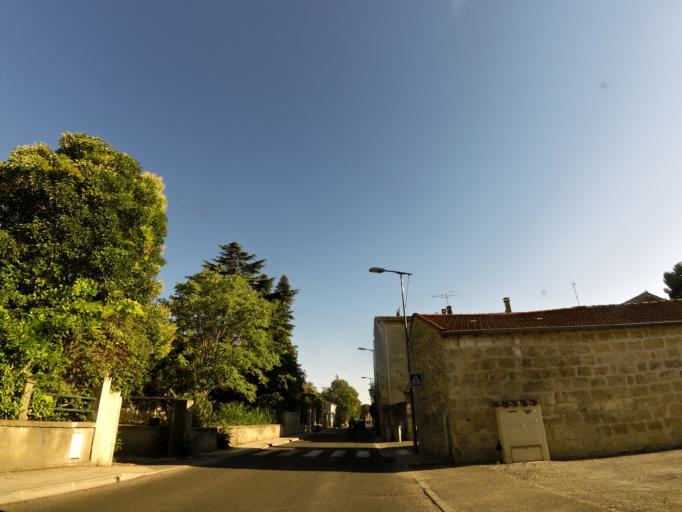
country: FR
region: Languedoc-Roussillon
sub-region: Departement du Gard
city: Sommieres
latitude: 43.7901
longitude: 4.0904
